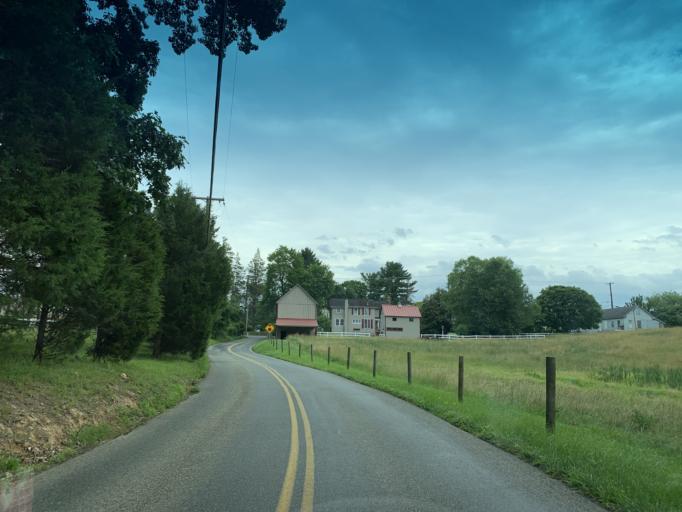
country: US
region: Maryland
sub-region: Harford County
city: Fallston
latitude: 39.5290
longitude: -76.4110
